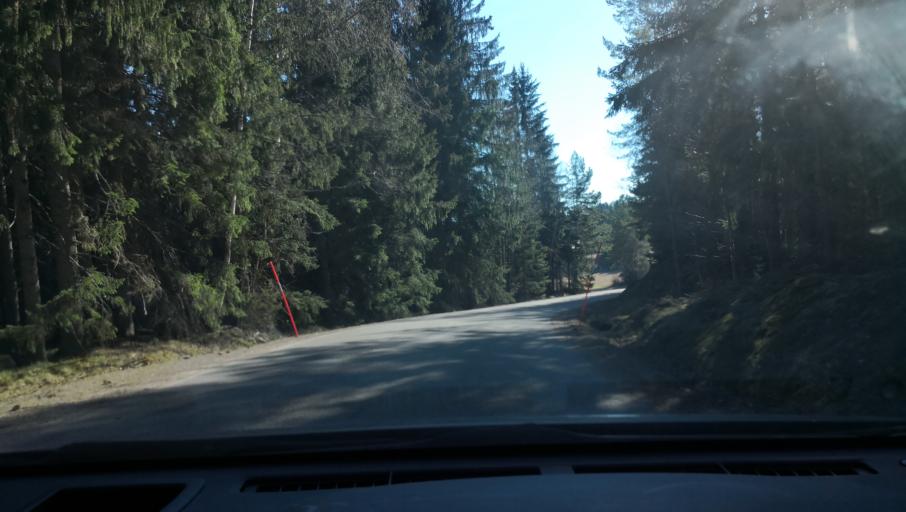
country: SE
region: Dalarna
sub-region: Avesta Kommun
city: Horndal
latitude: 60.0867
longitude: 16.4018
